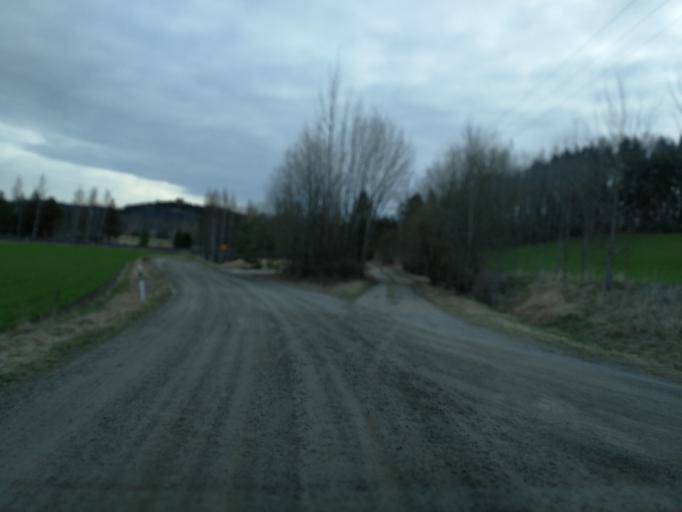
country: FI
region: Varsinais-Suomi
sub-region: Salo
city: Halikko
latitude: 60.3946
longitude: 23.0641
